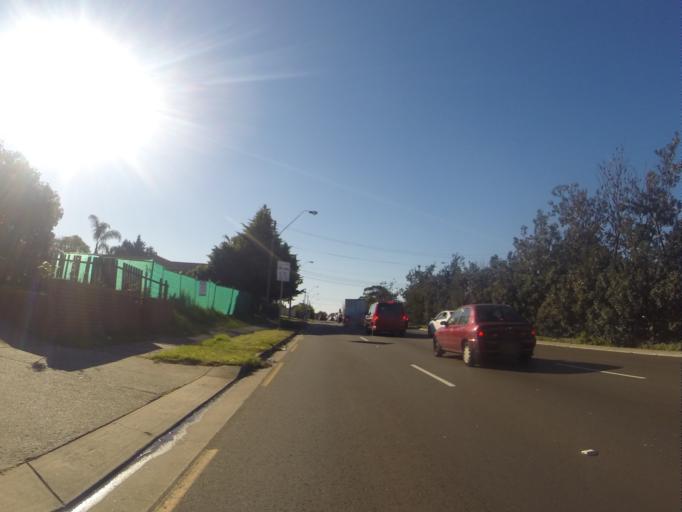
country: AU
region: New South Wales
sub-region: Canterbury
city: Lakemba
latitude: -33.9111
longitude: 151.0636
